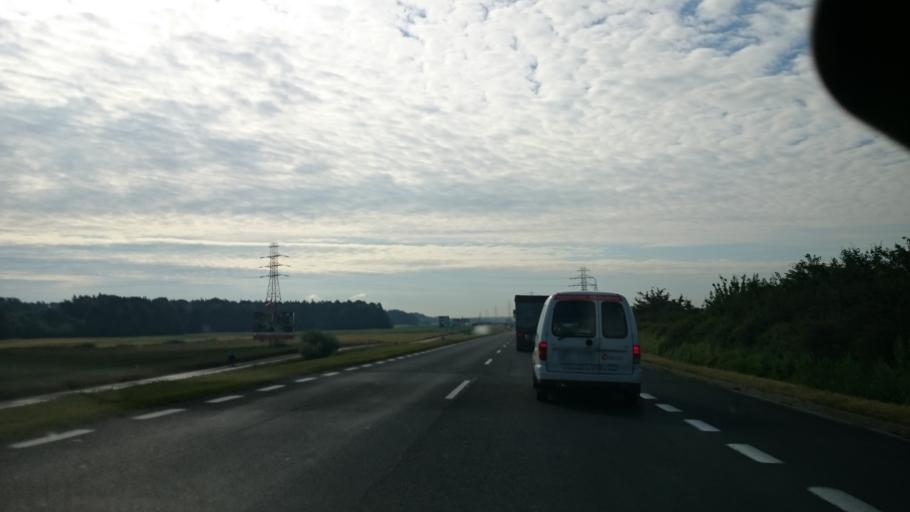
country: PL
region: Opole Voivodeship
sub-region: Powiat opolski
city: Opole
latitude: 50.6934
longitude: 17.9646
